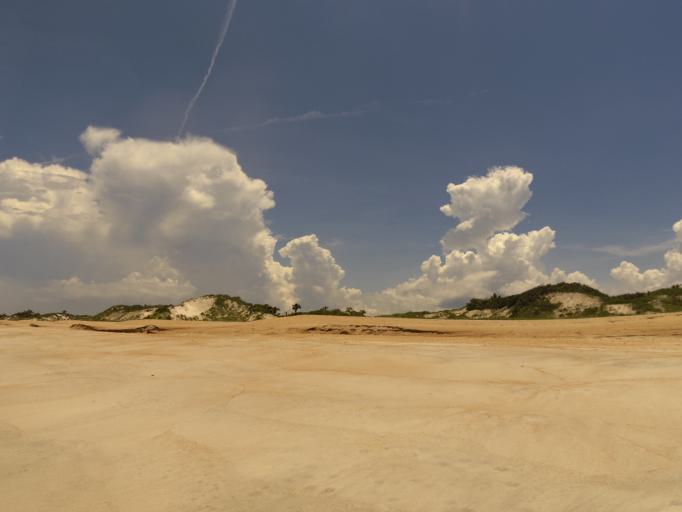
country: US
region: Florida
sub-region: Saint Johns County
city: Palm Valley
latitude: 30.1227
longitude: -81.3459
